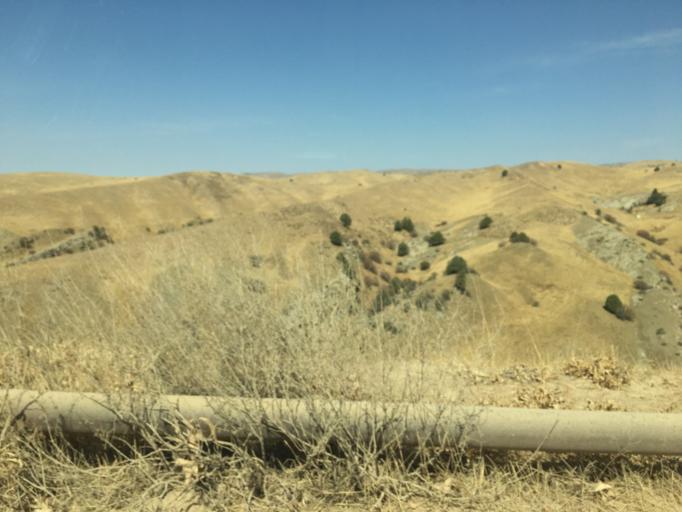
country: TM
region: Ahal
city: Baharly
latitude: 38.2741
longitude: 56.8988
